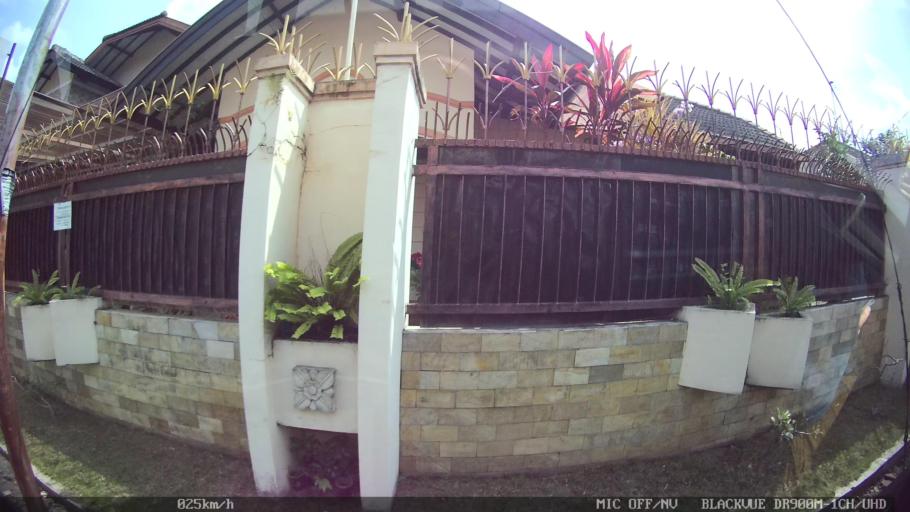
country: ID
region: Daerah Istimewa Yogyakarta
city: Yogyakarta
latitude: -7.7844
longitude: 110.3862
